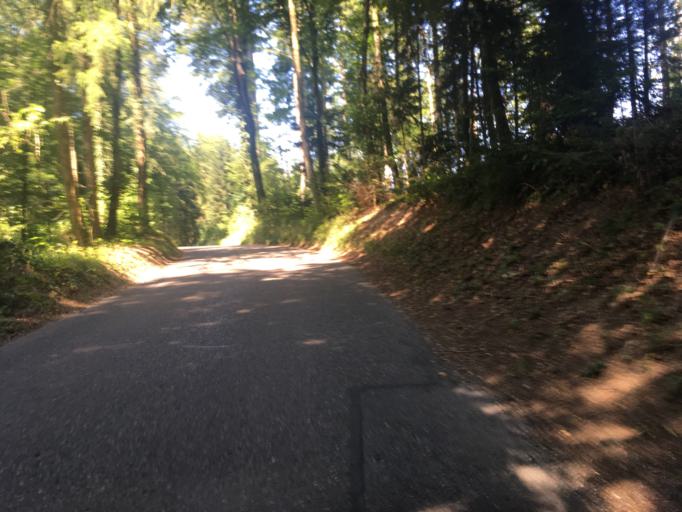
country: CH
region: Bern
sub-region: Bern-Mittelland District
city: Fraubrunnen
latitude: 47.0885
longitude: 7.5038
